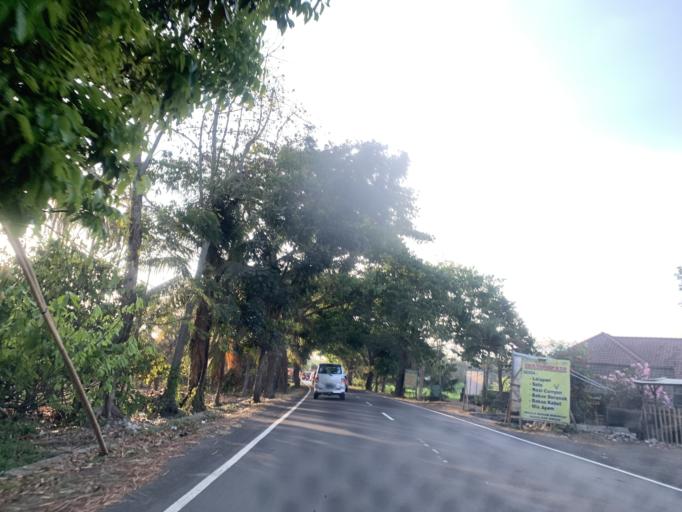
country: ID
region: Bali
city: Banjar Delodrurung
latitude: -8.4896
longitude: 114.9524
